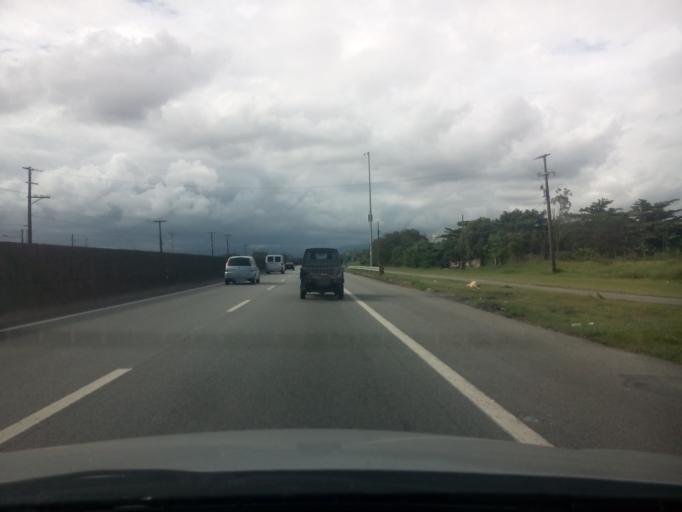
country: BR
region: Sao Paulo
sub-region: Guaruja
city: Guaruja
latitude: -23.9773
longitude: -46.2674
